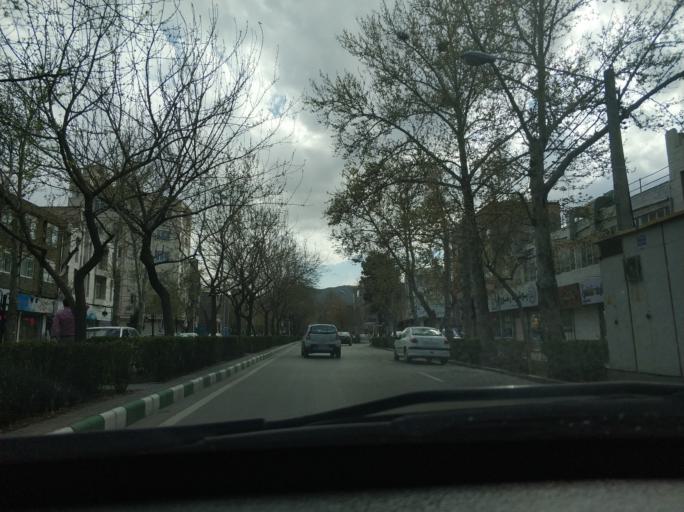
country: IR
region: Razavi Khorasan
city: Mashhad
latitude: 36.2734
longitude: 59.5909
